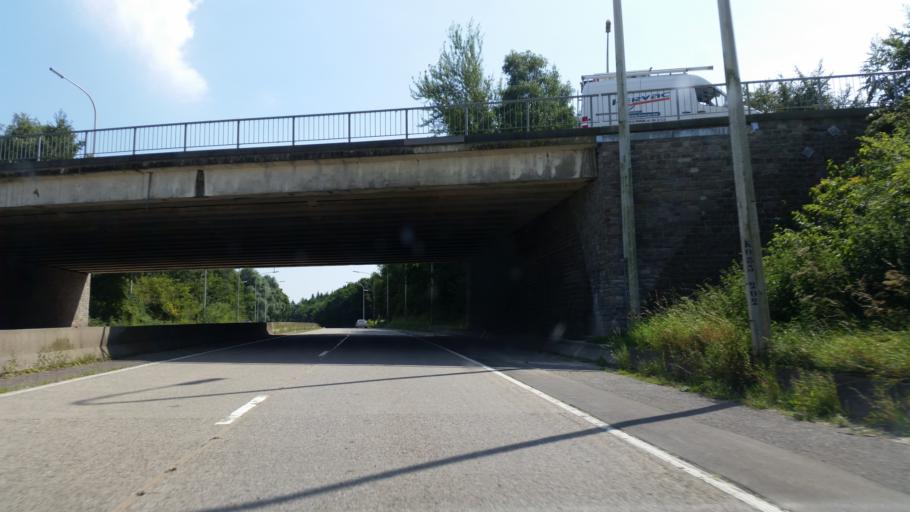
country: BE
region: Wallonia
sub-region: Province de Namur
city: Hamois
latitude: 50.2852
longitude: 5.1823
